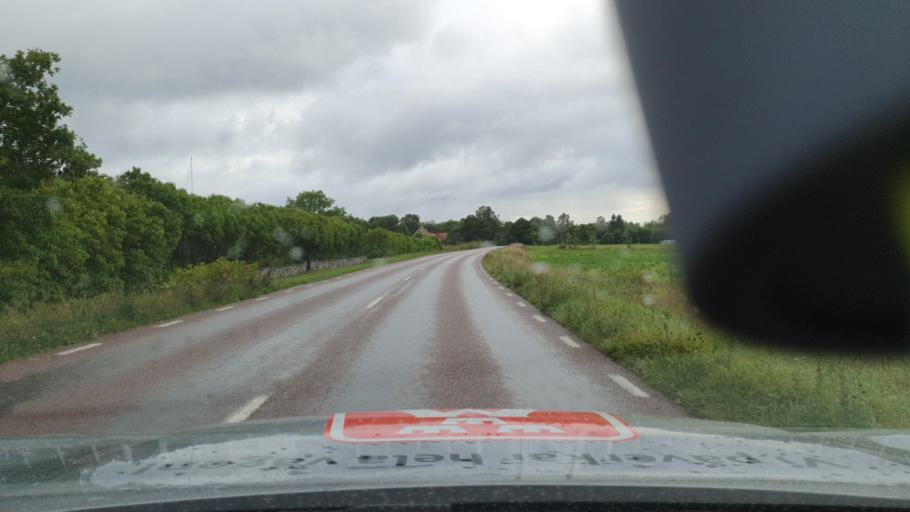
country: SE
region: Gotland
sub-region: Gotland
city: Hemse
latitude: 57.1322
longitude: 18.3432
